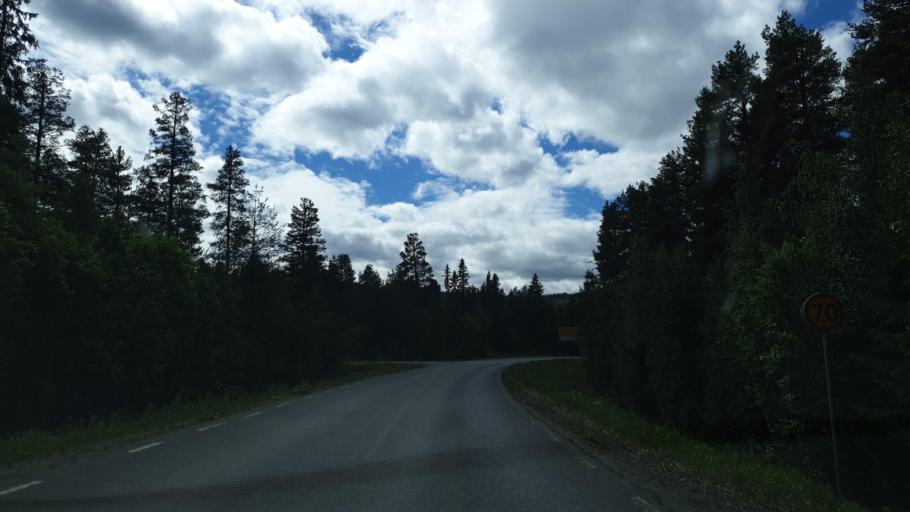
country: SE
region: Vaesterbotten
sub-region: Vilhelmina Kommun
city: Sjoberg
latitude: 64.9406
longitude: 15.8657
